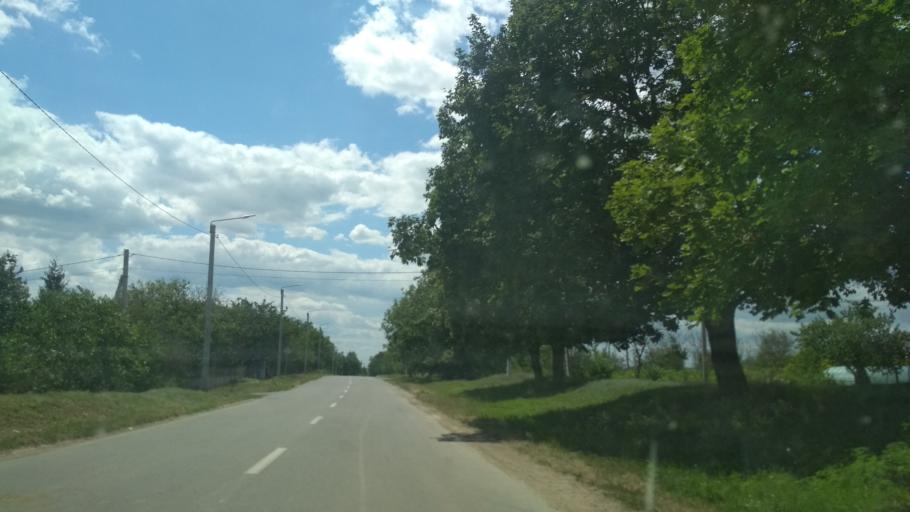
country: MD
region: Criuleni
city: Criuleni
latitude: 47.1737
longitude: 29.1956
